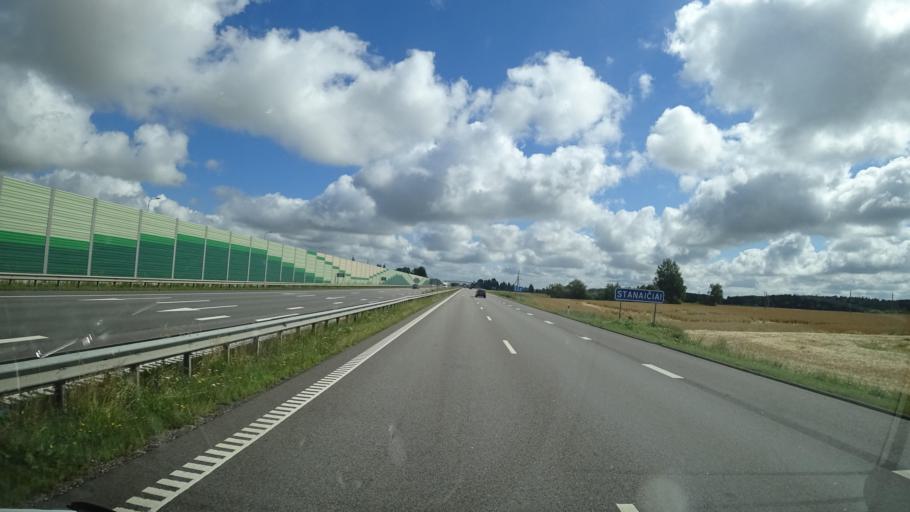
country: LT
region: Kauno apskritis
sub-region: Kauno rajonas
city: Mastaiciai
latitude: 54.7996
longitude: 23.8281
